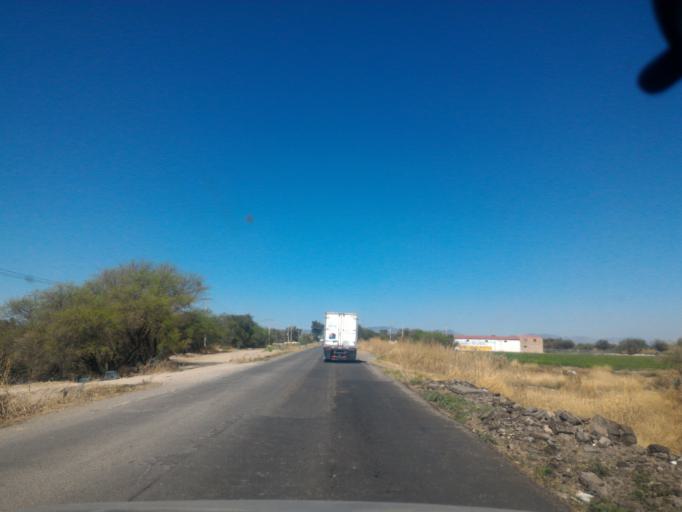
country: MX
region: Guanajuato
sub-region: San Francisco del Rincon
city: San Roque de Montes
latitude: 21.0276
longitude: -101.7824
